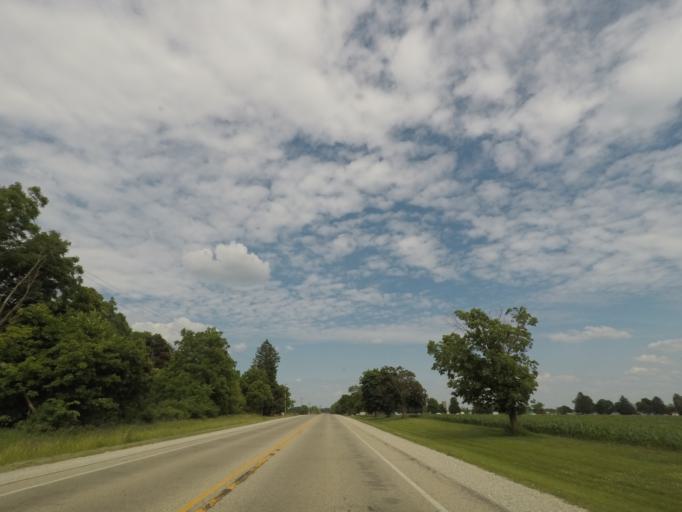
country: US
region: Wisconsin
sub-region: Walworth County
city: Whitewater
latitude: 42.8274
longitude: -88.7847
